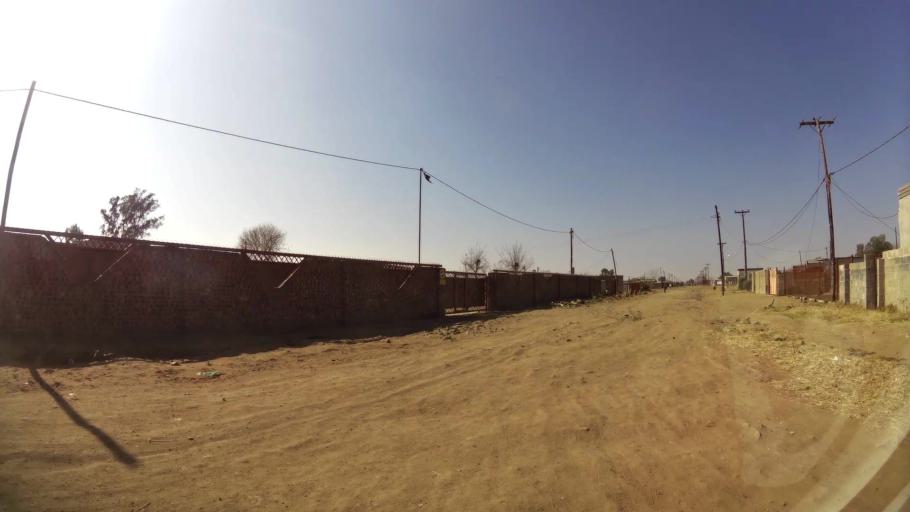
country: ZA
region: Orange Free State
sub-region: Mangaung Metropolitan Municipality
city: Bloemfontein
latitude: -29.1733
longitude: 26.2897
